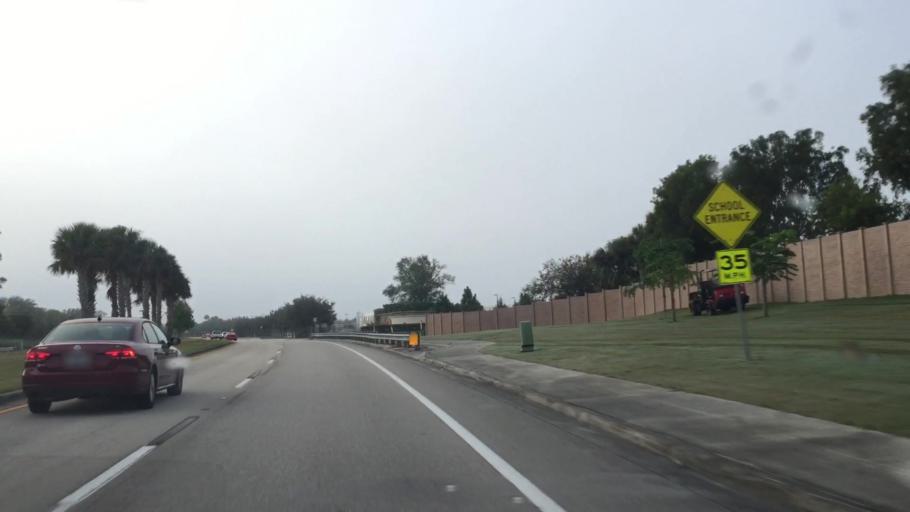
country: US
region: Florida
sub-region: Lee County
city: Gateway
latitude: 26.5884
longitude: -81.7845
